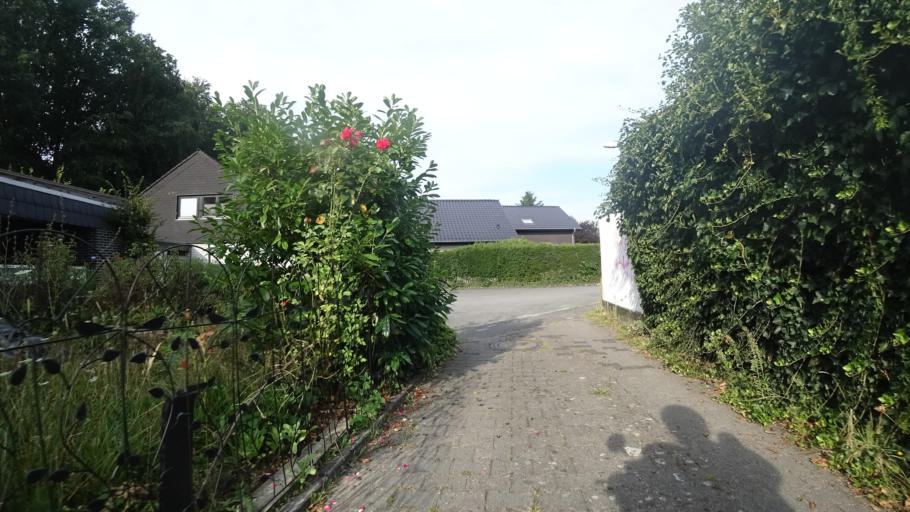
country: DE
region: North Rhine-Westphalia
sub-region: Regierungsbezirk Detmold
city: Guetersloh
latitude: 51.9431
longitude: 8.4072
